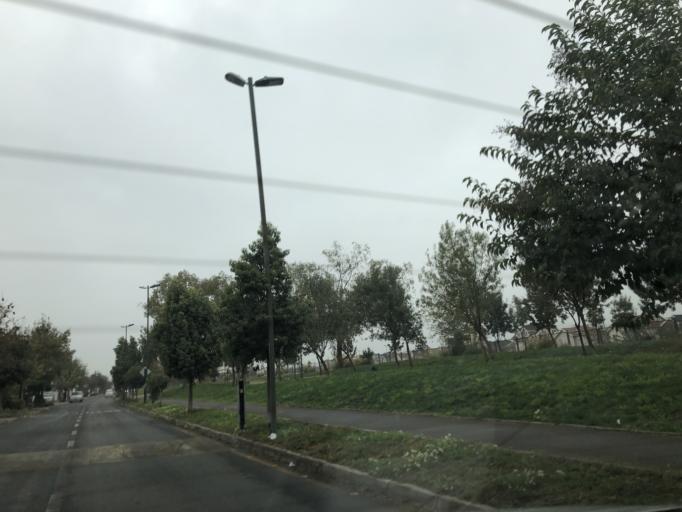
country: CL
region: Santiago Metropolitan
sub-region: Provincia de Cordillera
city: Puente Alto
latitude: -33.5963
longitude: -70.5932
